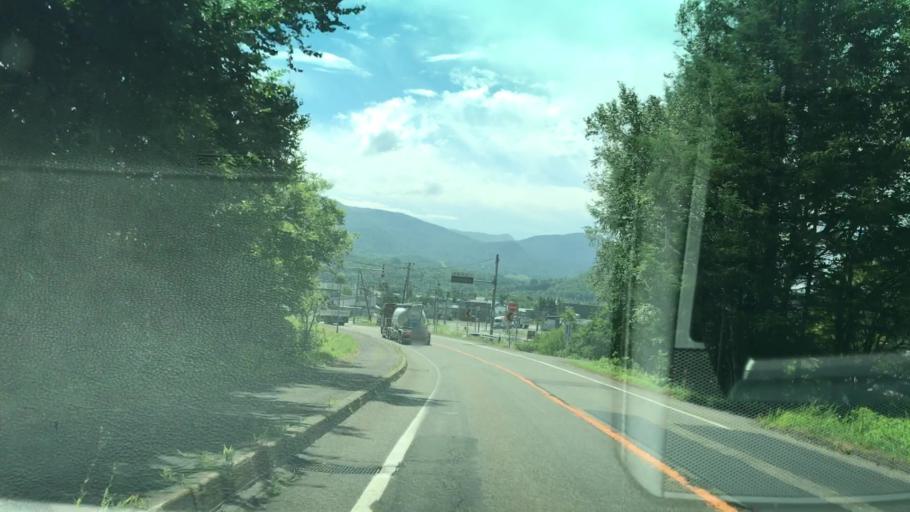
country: JP
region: Hokkaido
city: Shimo-furano
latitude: 42.8839
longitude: 142.4342
